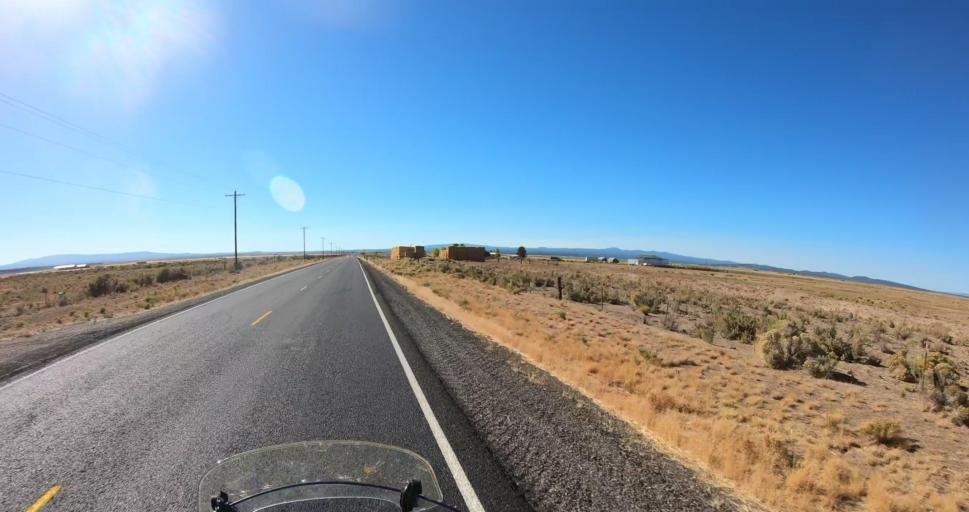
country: US
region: Oregon
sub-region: Deschutes County
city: La Pine
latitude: 43.1284
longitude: -120.9725
